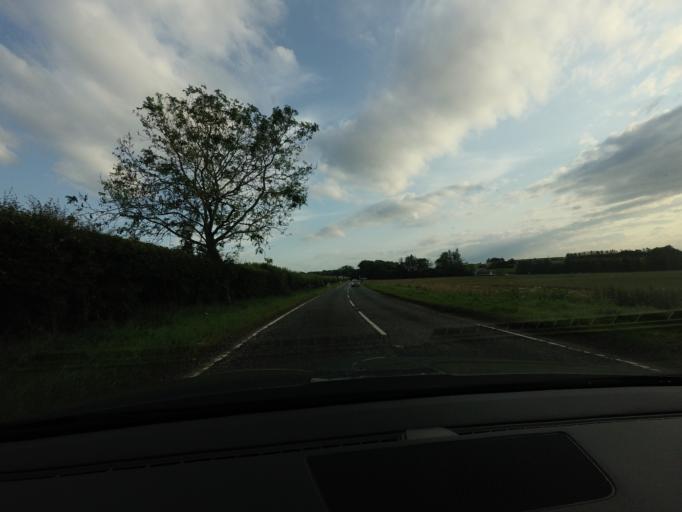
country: GB
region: Scotland
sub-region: Aberdeenshire
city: Turriff
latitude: 57.5470
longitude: -2.4434
